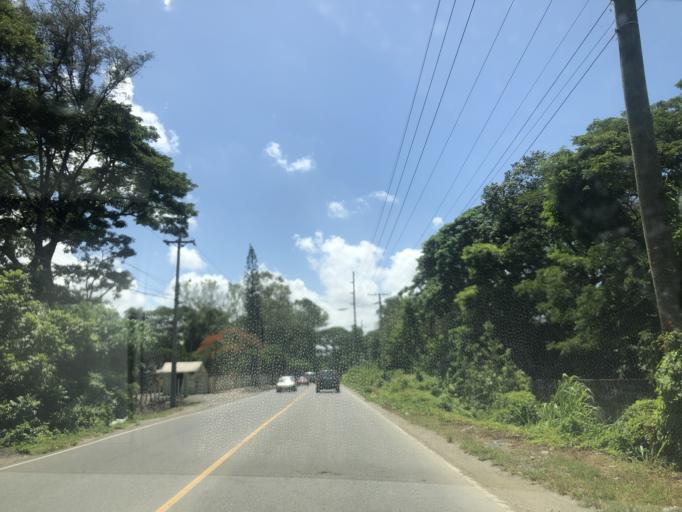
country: DO
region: Santiago
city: Santiago de los Caballeros
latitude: 19.4521
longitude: -70.7480
